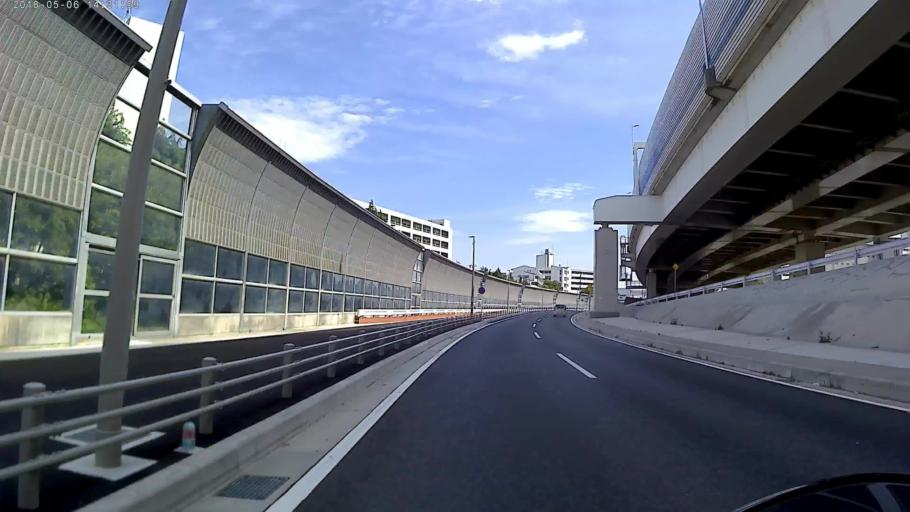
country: JP
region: Kanagawa
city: Yokohama
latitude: 35.4293
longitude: 139.6715
